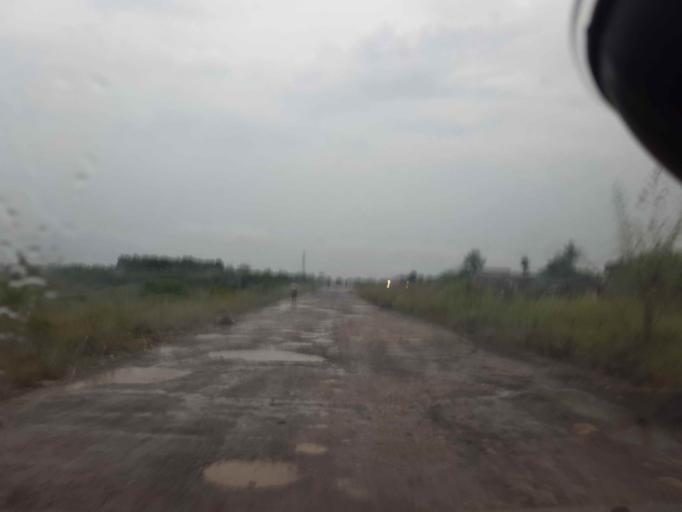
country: ID
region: Lampung
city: Kedaton
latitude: -5.3737
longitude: 105.3185
